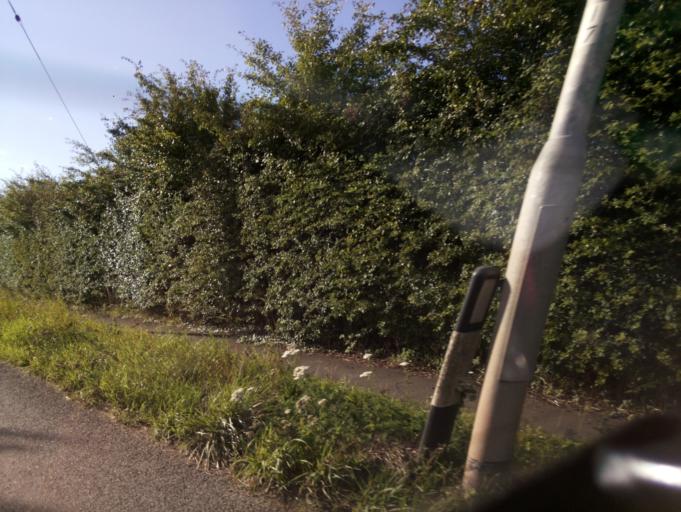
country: GB
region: England
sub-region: Devon
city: Newton Poppleford
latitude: 50.6981
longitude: -3.3068
